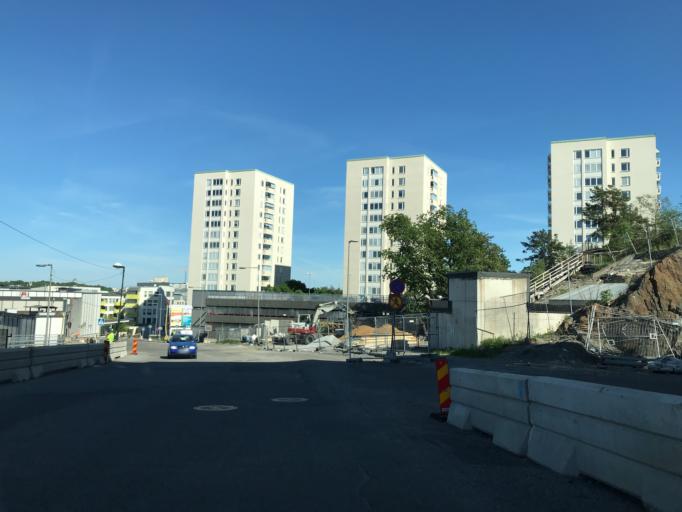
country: SE
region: Stockholm
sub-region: Stockholms Kommun
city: Arsta
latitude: 59.3090
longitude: 18.0197
